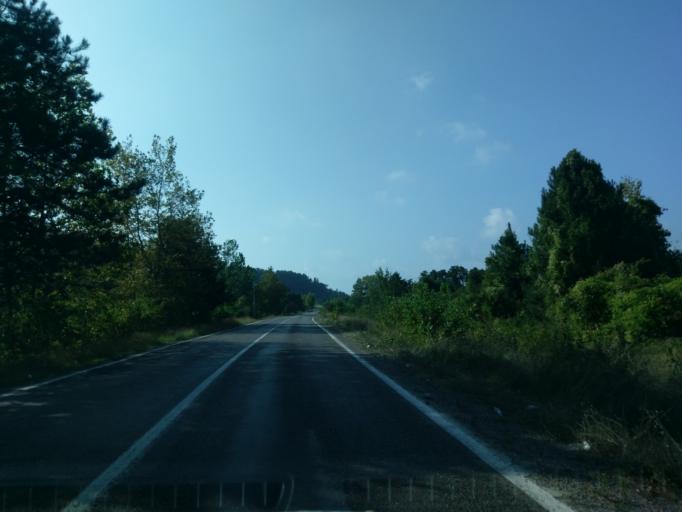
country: TR
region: Sinop
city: Yenikonak
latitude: 41.9391
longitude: 34.7219
